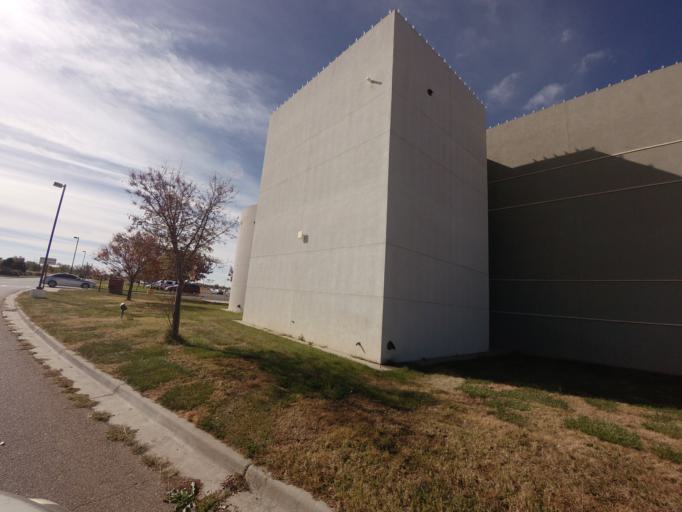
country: US
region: New Mexico
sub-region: Curry County
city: Clovis
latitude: 34.4203
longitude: -103.2357
